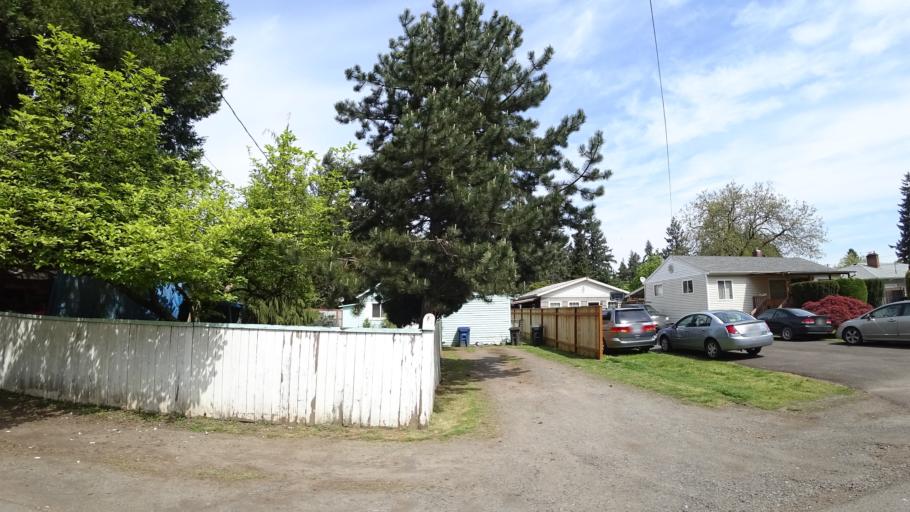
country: US
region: Oregon
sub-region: Clackamas County
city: Milwaukie
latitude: 45.4532
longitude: -122.6025
